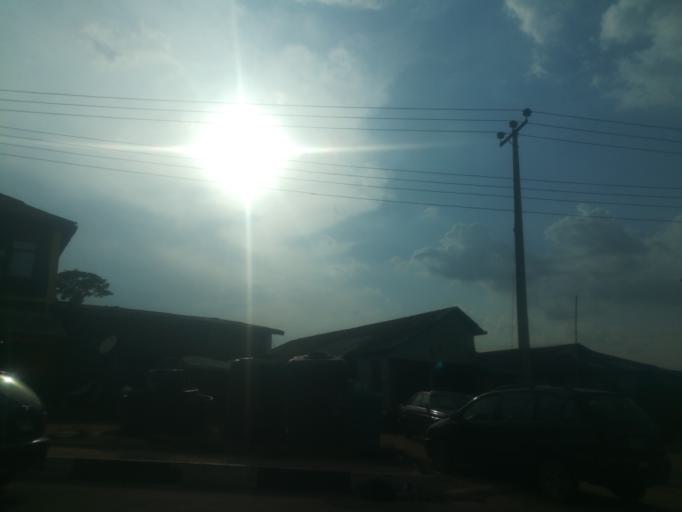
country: NG
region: Ogun
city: Abeokuta
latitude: 7.1462
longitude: 3.3300
